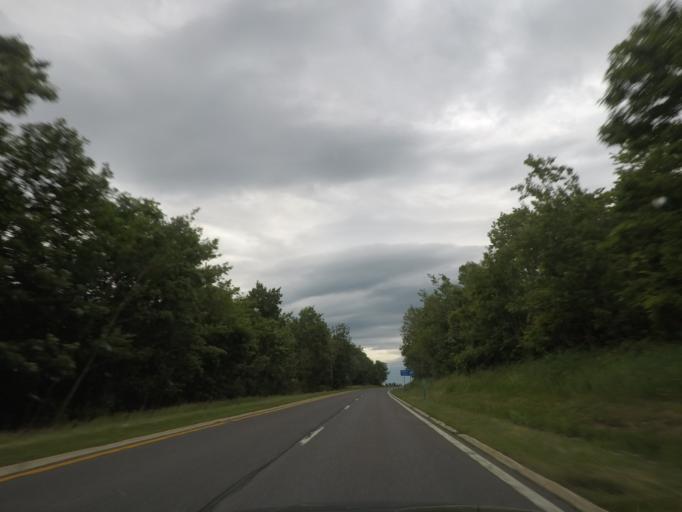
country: US
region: New York
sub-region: Dutchess County
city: Pine Plains
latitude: 42.0664
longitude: -73.7262
